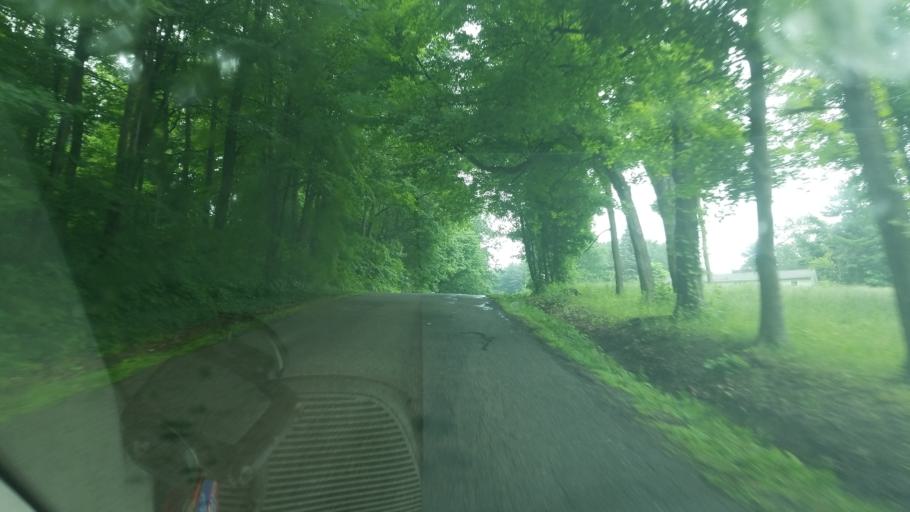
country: US
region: Ohio
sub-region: Sandusky County
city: Bellville
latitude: 40.6449
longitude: -82.4952
